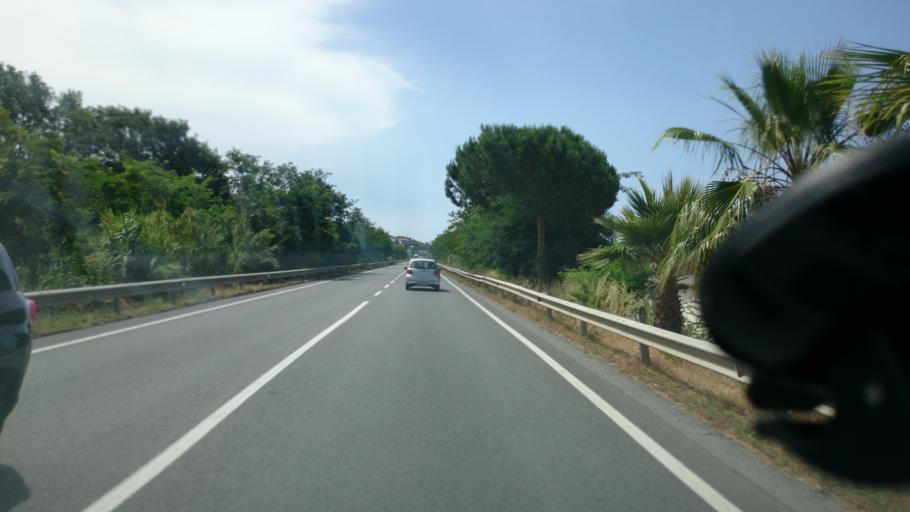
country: IT
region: Calabria
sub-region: Provincia di Cosenza
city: Diamante
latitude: 39.6909
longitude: 15.8173
